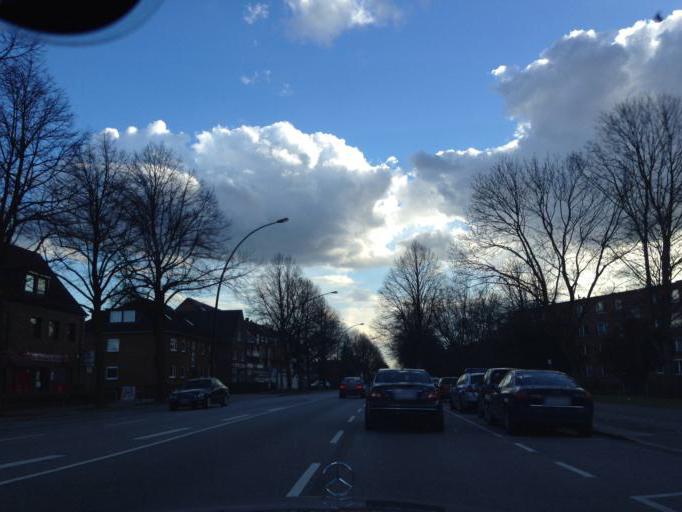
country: DE
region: Hamburg
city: Wandsbek
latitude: 53.5471
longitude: 10.1067
